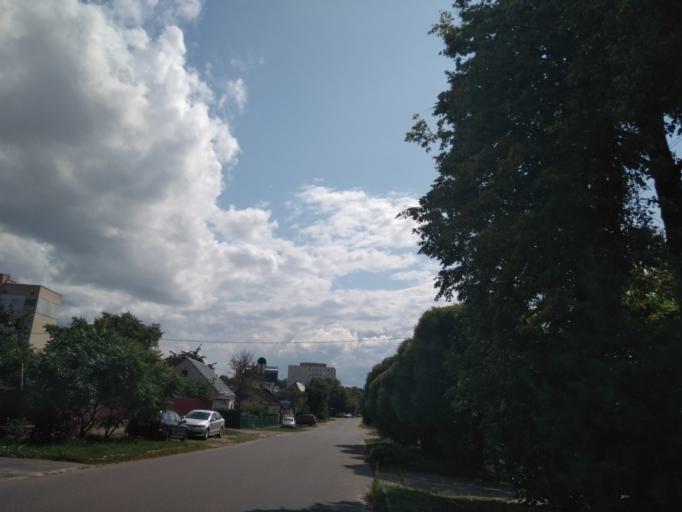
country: BY
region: Minsk
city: Minsk
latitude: 53.9367
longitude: 27.5555
